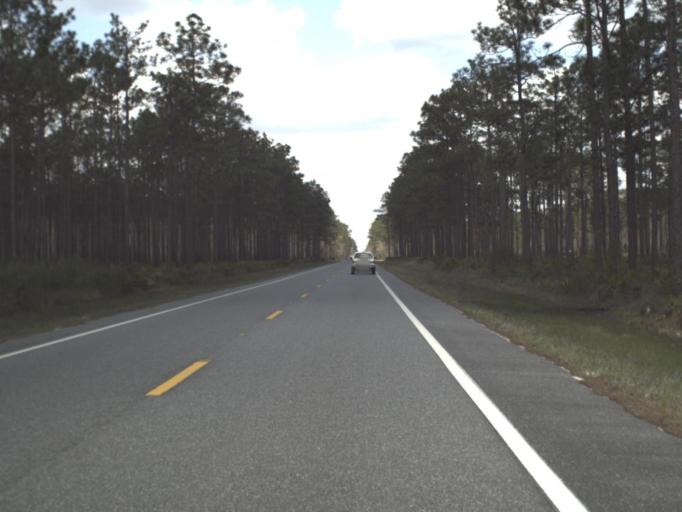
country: US
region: Florida
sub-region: Franklin County
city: Apalachicola
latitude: 29.9833
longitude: -84.9757
